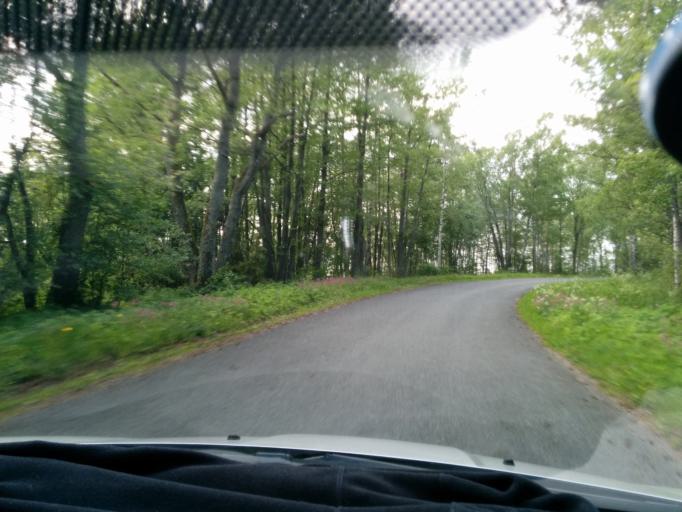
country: EE
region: Harju
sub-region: Loksa linn
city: Loksa
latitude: 59.6172
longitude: 25.6863
